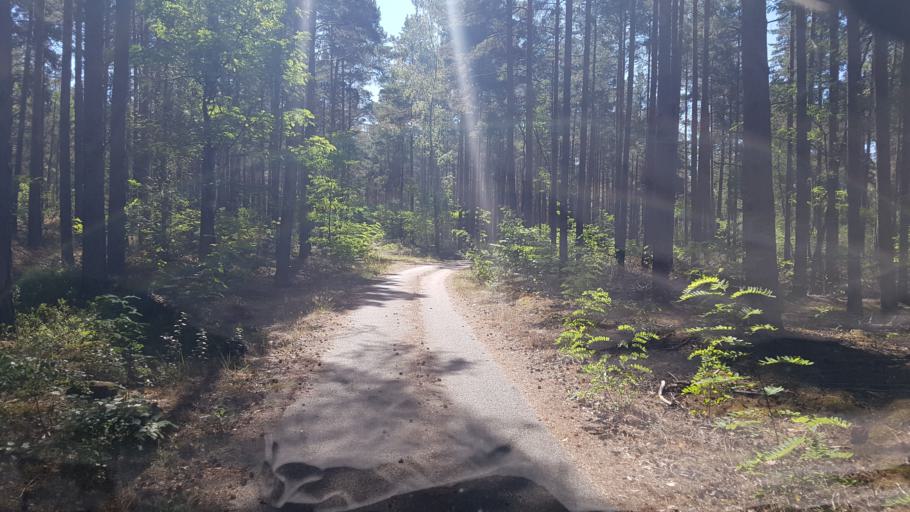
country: DE
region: Brandenburg
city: Calau
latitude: 51.7059
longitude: 13.9992
